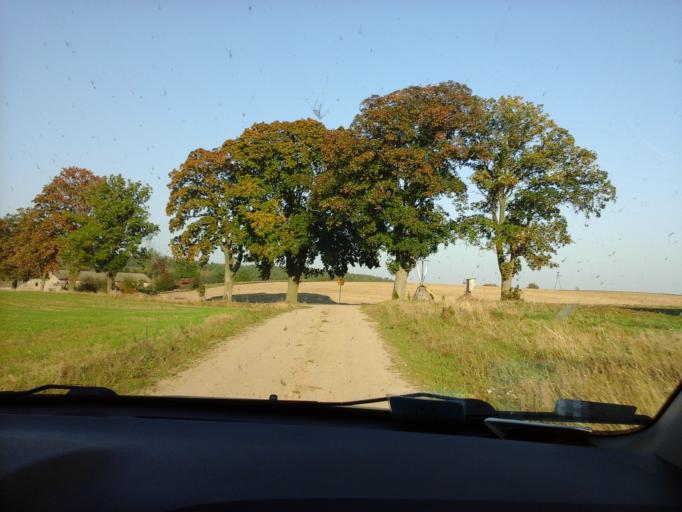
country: PL
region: Kujawsko-Pomorskie
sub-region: Powiat brodnicki
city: Bartniczka
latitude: 53.2825
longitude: 19.6908
